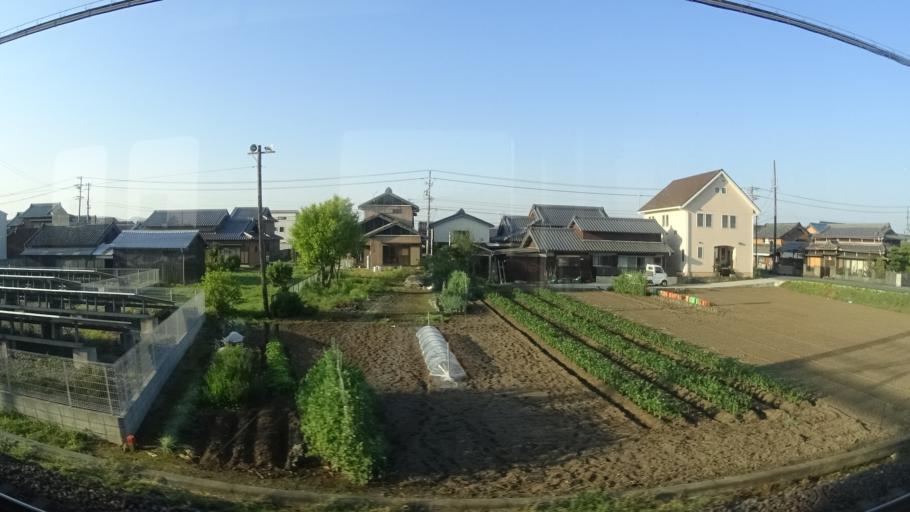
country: JP
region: Mie
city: Ise
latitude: 34.5372
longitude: 136.6231
